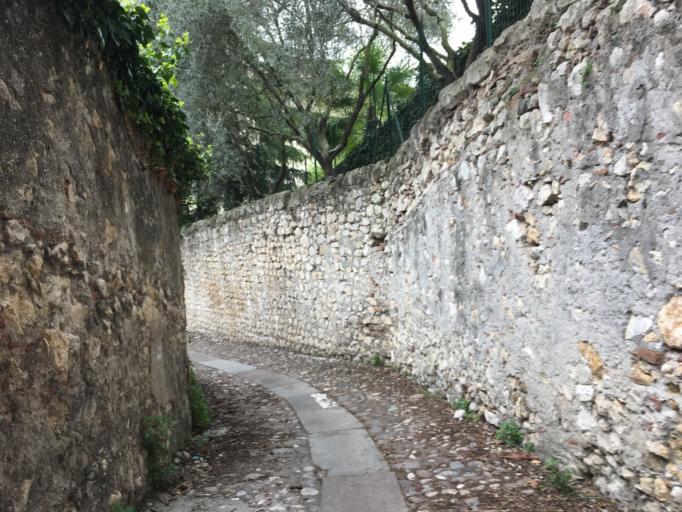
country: IT
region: Veneto
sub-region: Provincia di Verona
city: Verona
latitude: 45.4511
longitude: 10.9967
